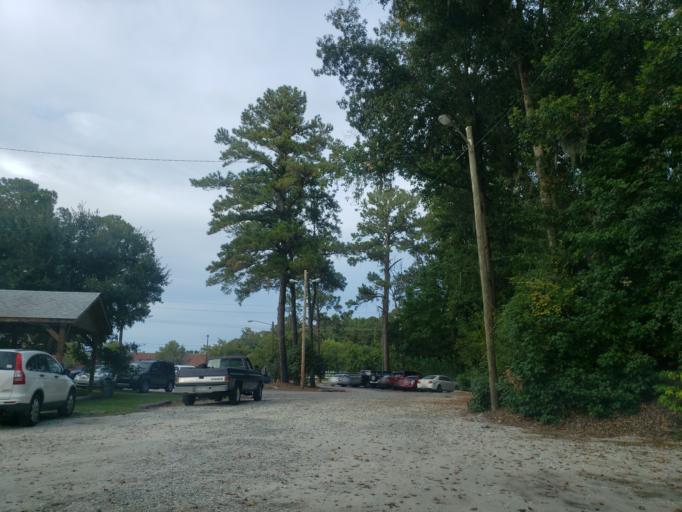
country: US
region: Georgia
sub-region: Chatham County
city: Isle of Hope
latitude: 32.0039
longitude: -81.0943
